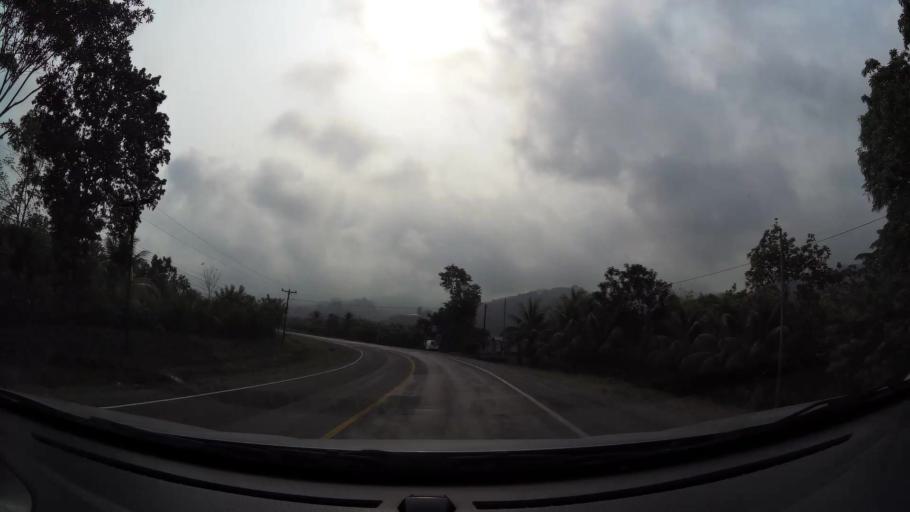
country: HN
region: Yoro
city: Toyos
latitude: 15.5544
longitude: -87.6306
